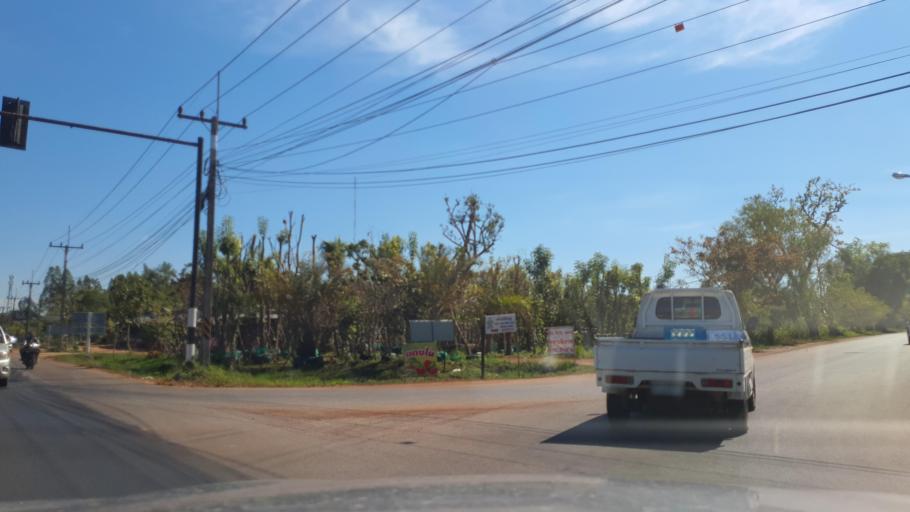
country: TH
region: Sakon Nakhon
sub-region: Amphoe Khok Si Suphan
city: Khok Si Suphan
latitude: 17.0697
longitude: 104.2152
